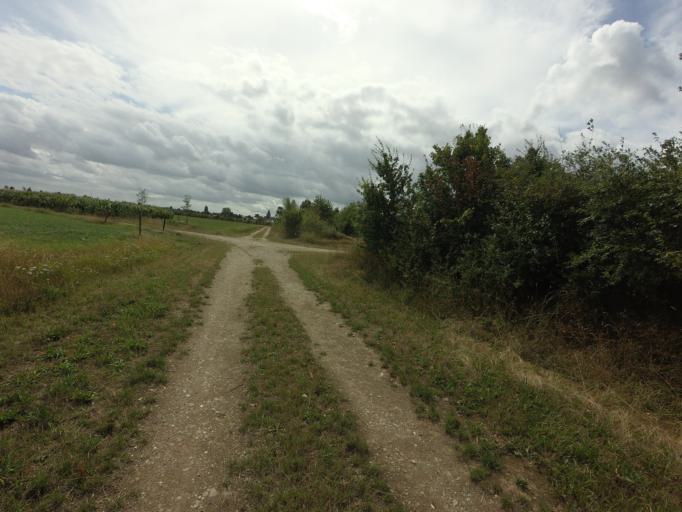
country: BE
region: Flanders
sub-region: Provincie Limburg
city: Maaseik
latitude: 51.1173
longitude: 5.8306
